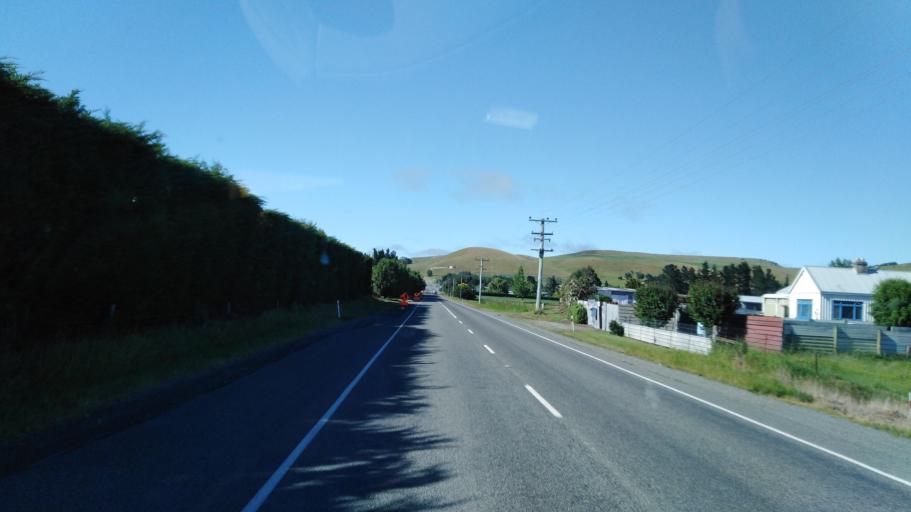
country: NZ
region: Canterbury
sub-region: Hurunui District
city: Amberley
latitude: -42.9631
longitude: 172.7075
